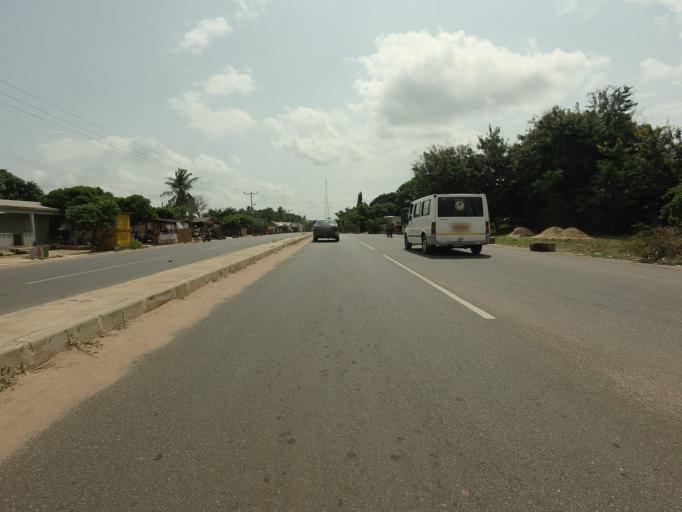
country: TG
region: Maritime
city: Lome
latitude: 6.2307
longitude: 1.0073
